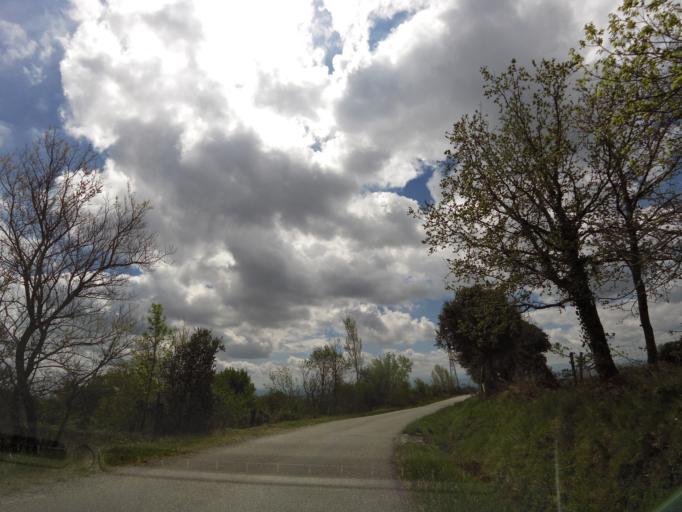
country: FR
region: Languedoc-Roussillon
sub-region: Departement de l'Aude
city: Villepinte
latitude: 43.3530
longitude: 2.0969
